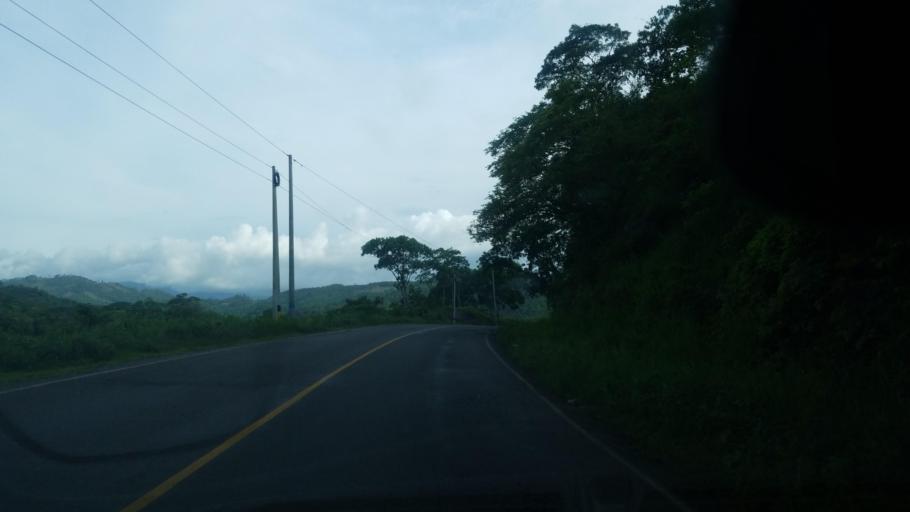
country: HN
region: Santa Barbara
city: Ilama
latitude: 15.1037
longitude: -88.1995
